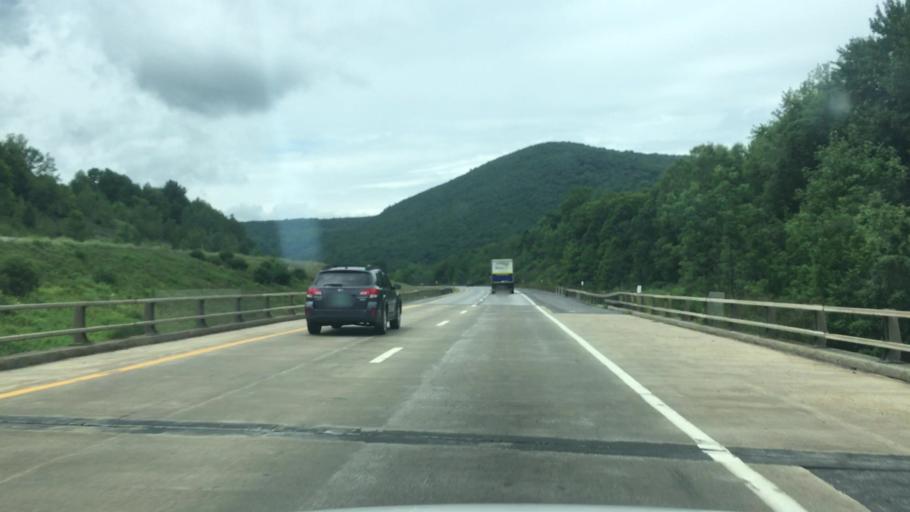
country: US
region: New York
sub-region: Otsego County
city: Worcester
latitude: 42.6498
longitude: -74.6233
